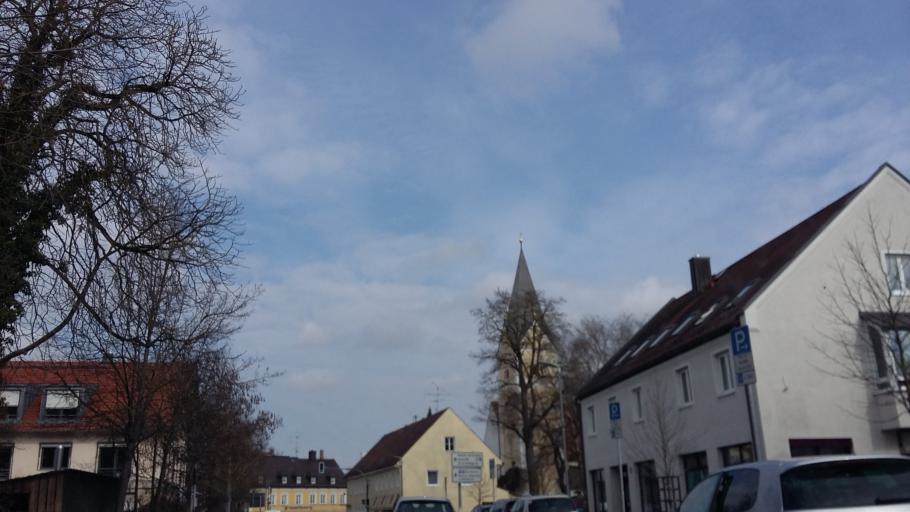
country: DE
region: Bavaria
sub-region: Upper Bavaria
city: Garching bei Munchen
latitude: 48.2480
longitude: 11.6508
